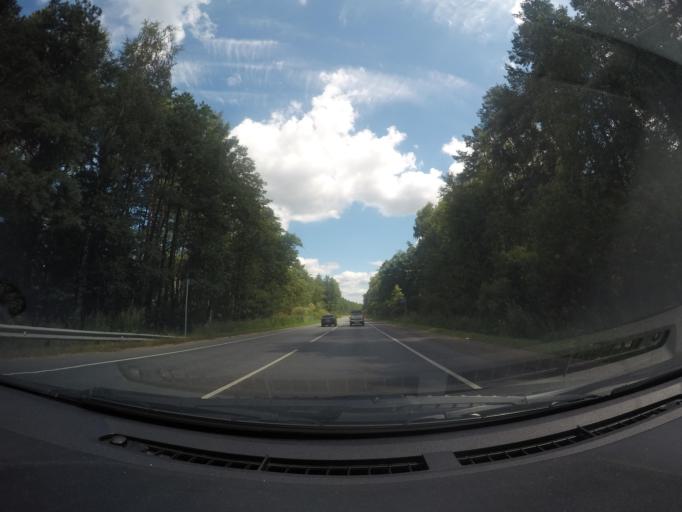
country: RU
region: Moskovskaya
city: Ramenskoye
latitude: 55.6389
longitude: 38.2426
